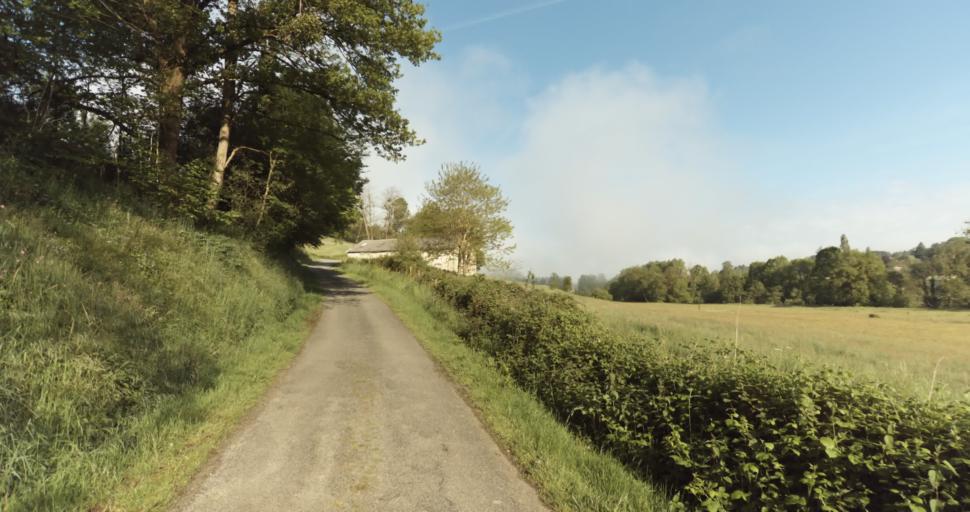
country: FR
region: Limousin
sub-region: Departement de la Haute-Vienne
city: Le Vigen
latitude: 45.7503
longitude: 1.2837
